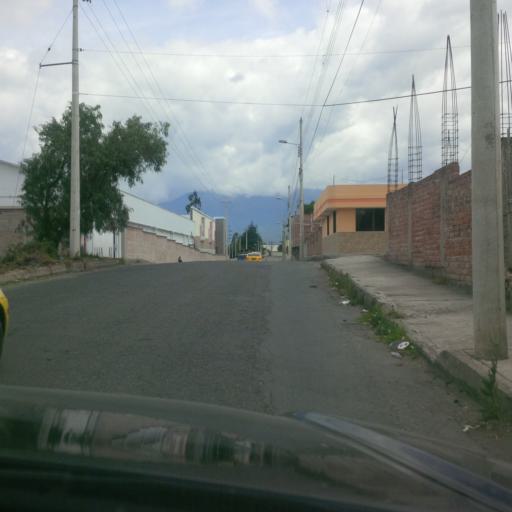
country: EC
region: Chimborazo
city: Riobamba
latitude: -1.6548
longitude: -78.6473
